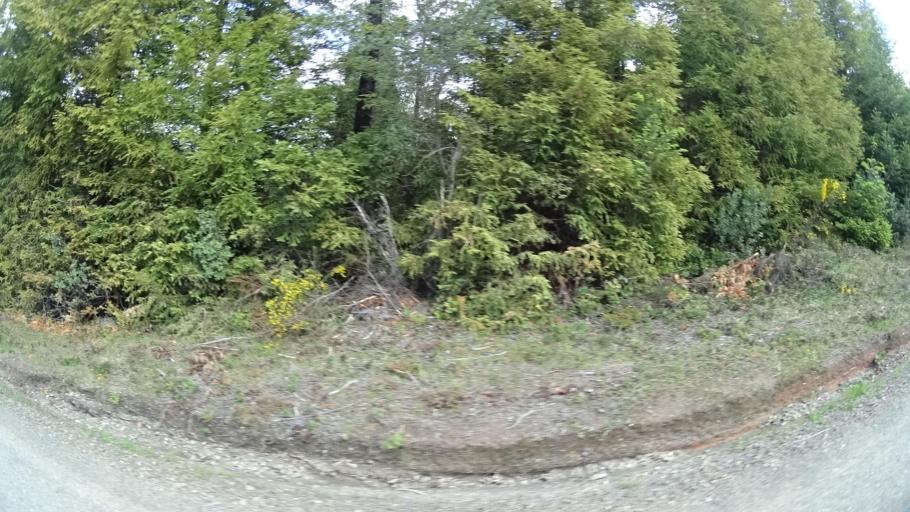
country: US
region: California
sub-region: Humboldt County
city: Blue Lake
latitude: 40.7711
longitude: -123.9596
